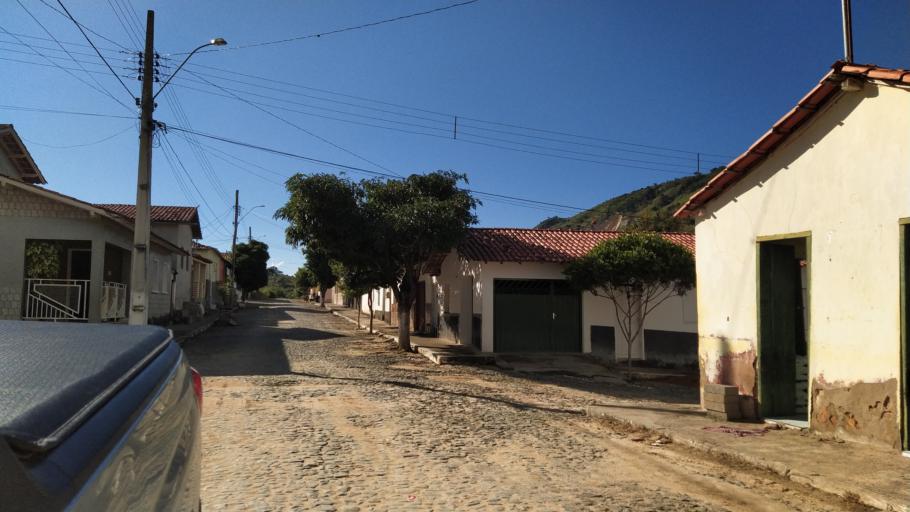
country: BR
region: Minas Gerais
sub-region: Almenara
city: Almenara
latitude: -16.5192
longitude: -40.4423
